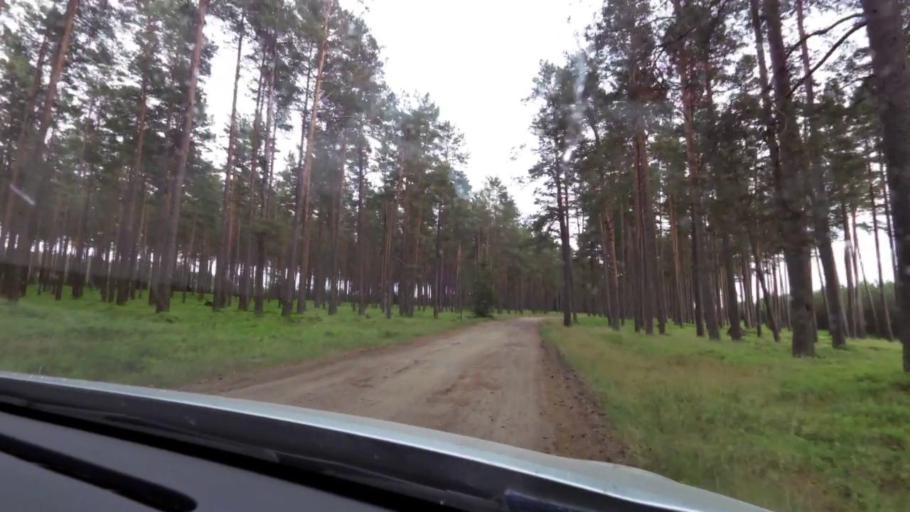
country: PL
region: Pomeranian Voivodeship
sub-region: Powiat bytowski
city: Trzebielino
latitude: 54.2093
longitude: 17.0056
